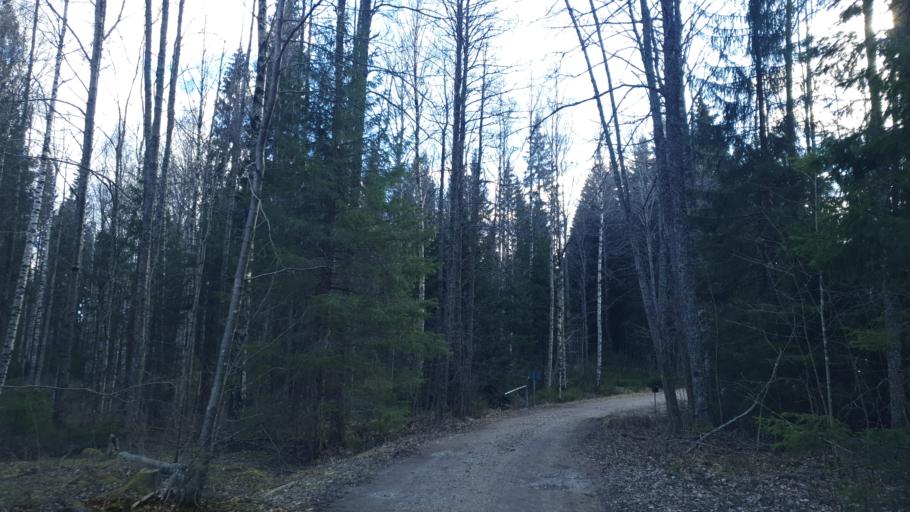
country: SE
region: OErebro
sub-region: Orebro Kommun
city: Garphyttan
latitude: 59.3685
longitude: 14.9679
